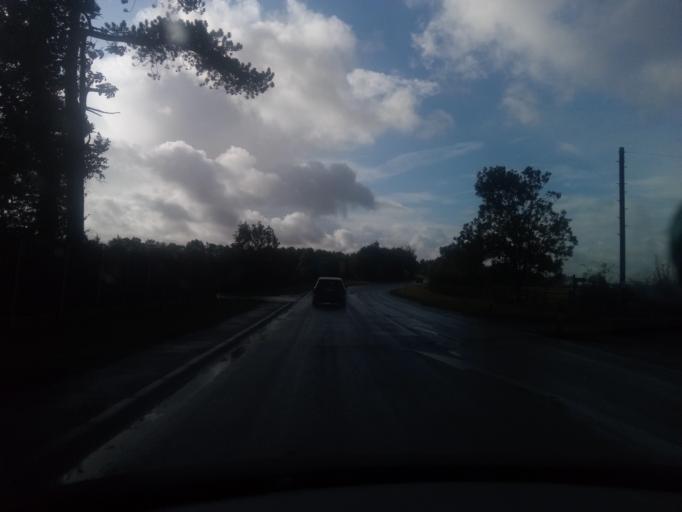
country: GB
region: England
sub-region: Cumbria
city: Carlisle
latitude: 54.9341
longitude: -2.9455
